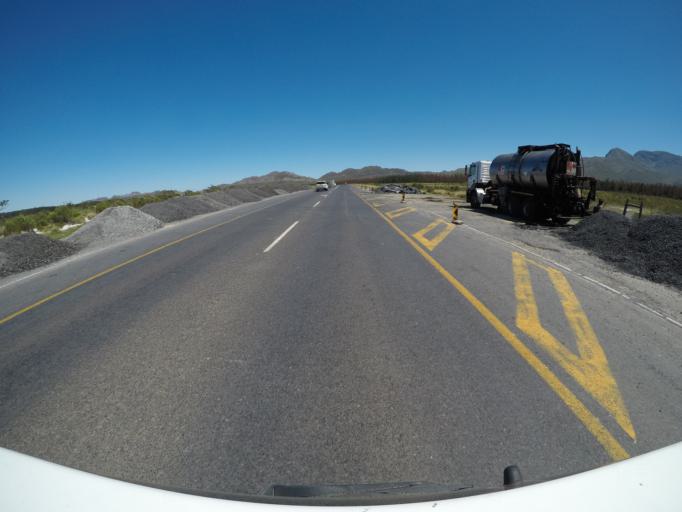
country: ZA
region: Western Cape
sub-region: Overberg District Municipality
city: Grabouw
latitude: -34.1550
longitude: 18.9697
